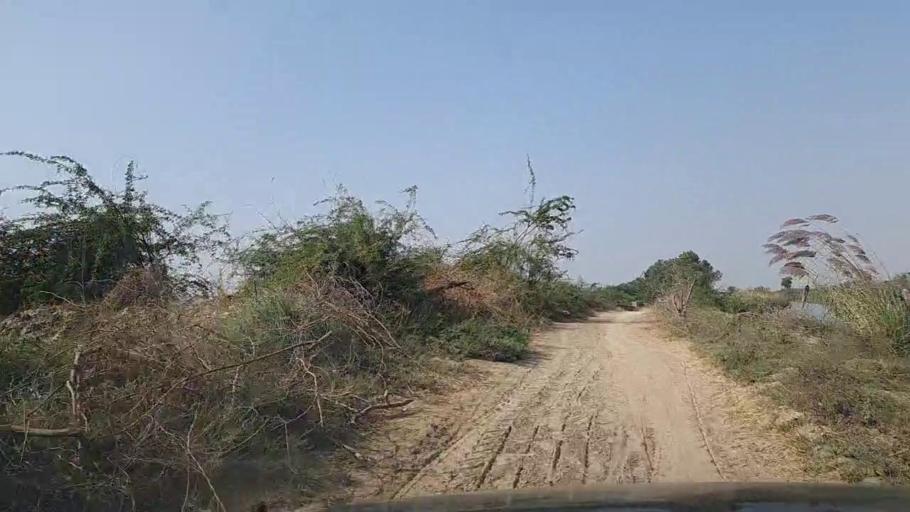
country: PK
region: Sindh
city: Gharo
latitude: 24.7279
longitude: 67.7049
